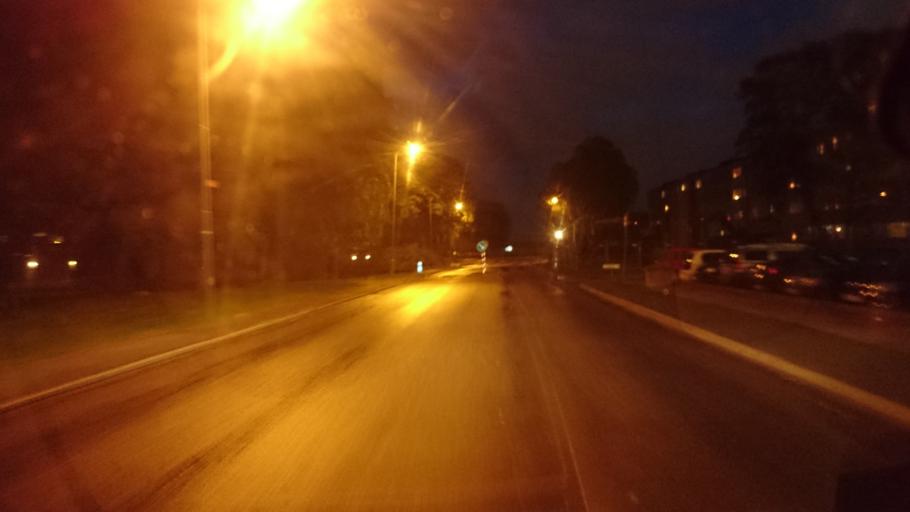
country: SE
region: Vaestra Goetaland
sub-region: Goteborg
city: Majorna
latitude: 57.6747
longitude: 11.9127
